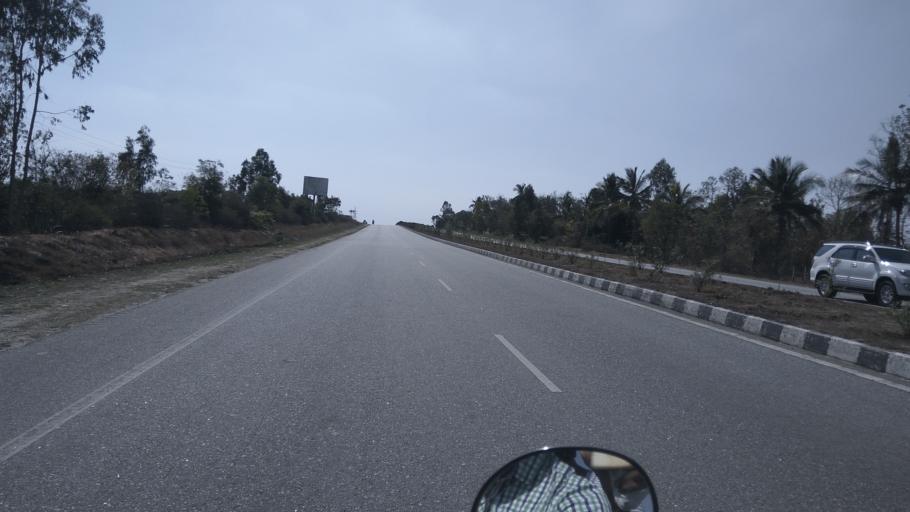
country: IN
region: Karnataka
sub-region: Kolar
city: Mulbagal
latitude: 13.1528
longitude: 78.3206
